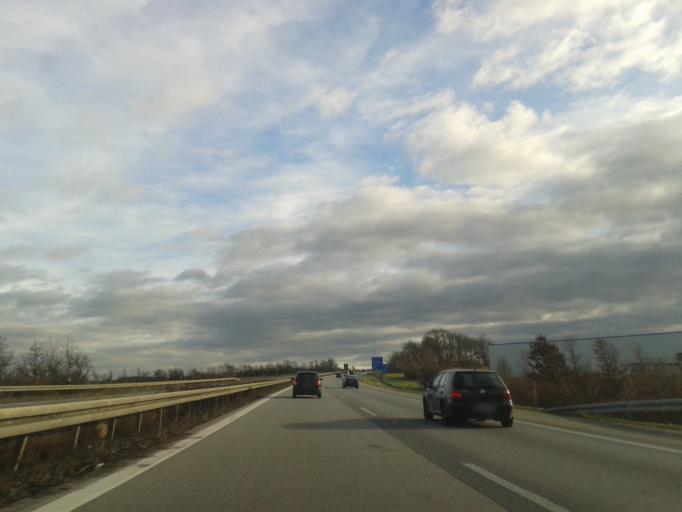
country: DE
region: Saxony
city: Goda
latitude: 51.1965
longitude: 14.3448
